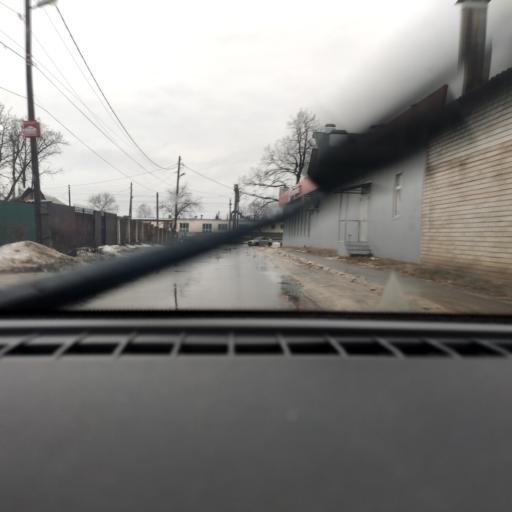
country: RU
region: Voronezj
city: Somovo
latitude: 51.7377
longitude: 39.3555
